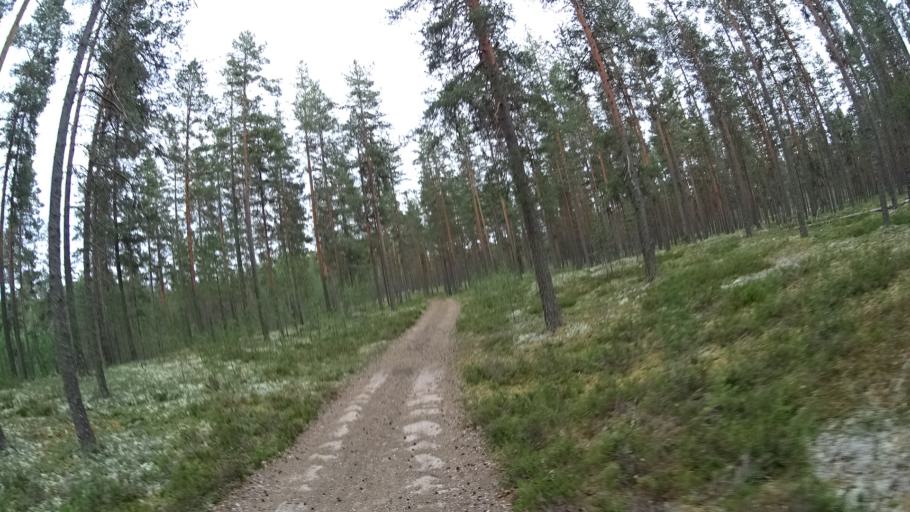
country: FI
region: Satakunta
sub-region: Pohjois-Satakunta
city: Jaemijaervi
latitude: 61.7624
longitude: 22.7545
